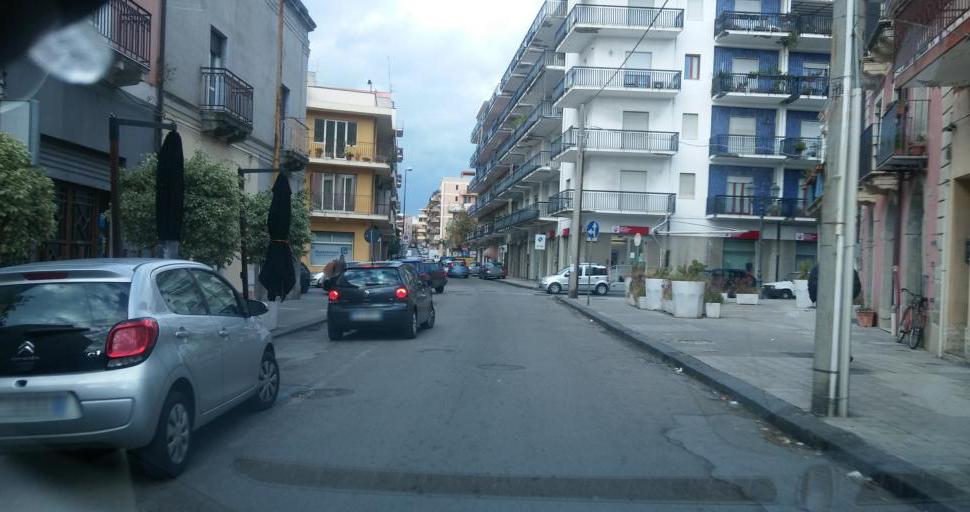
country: IT
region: Sicily
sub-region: Messina
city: Milazzo
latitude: 38.2193
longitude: 15.2402
